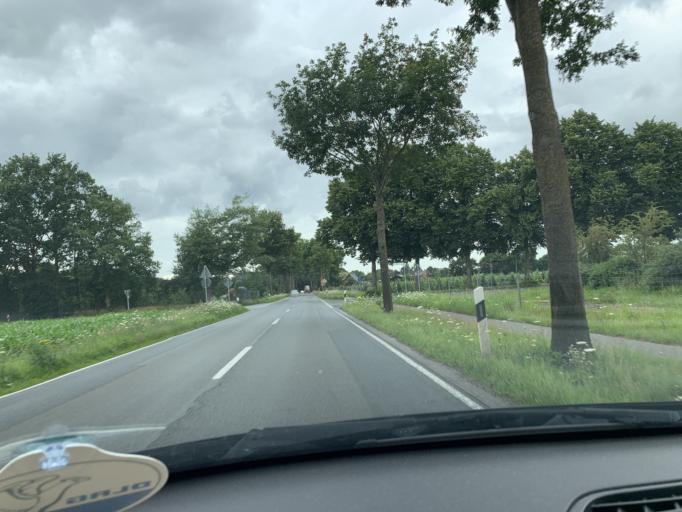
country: DE
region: Lower Saxony
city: Edewecht
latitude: 53.1264
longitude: 7.9094
